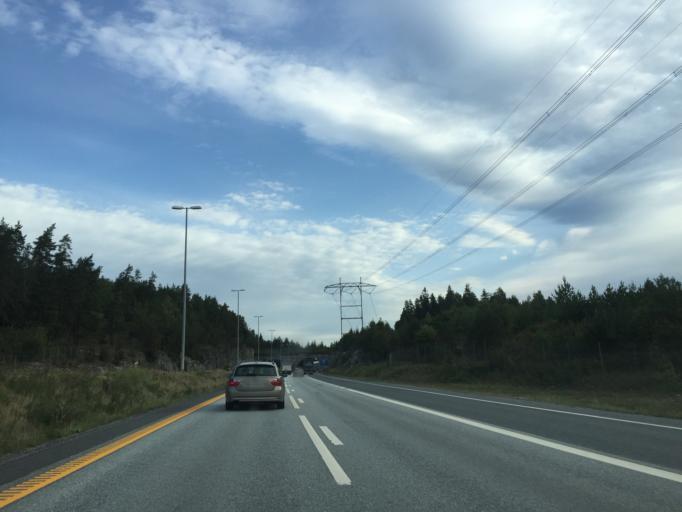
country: NO
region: Akershus
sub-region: Oppegard
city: Kolbotn
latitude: 59.7857
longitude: 10.8392
